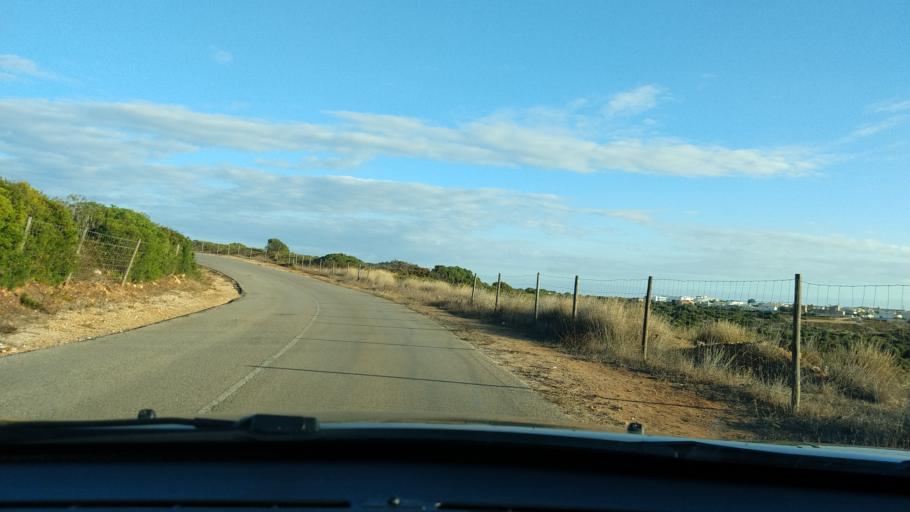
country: PT
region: Faro
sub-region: Vila do Bispo
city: Sagres
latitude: 37.0216
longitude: -8.9366
